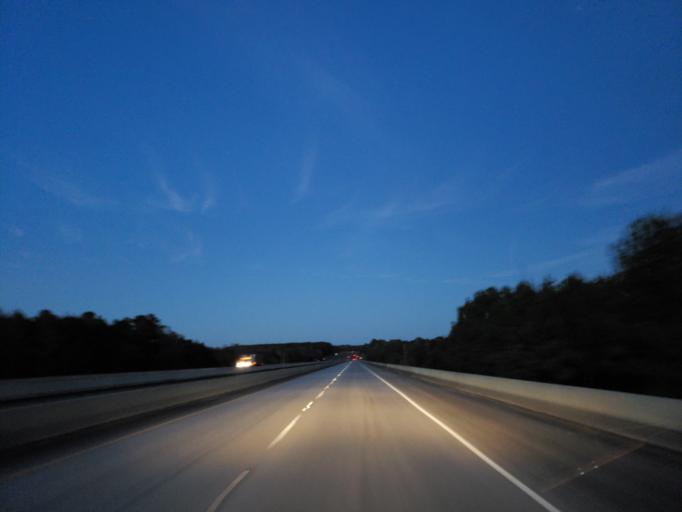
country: US
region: Mississippi
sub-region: Clarke County
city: Quitman
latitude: 31.9814
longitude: -88.7174
